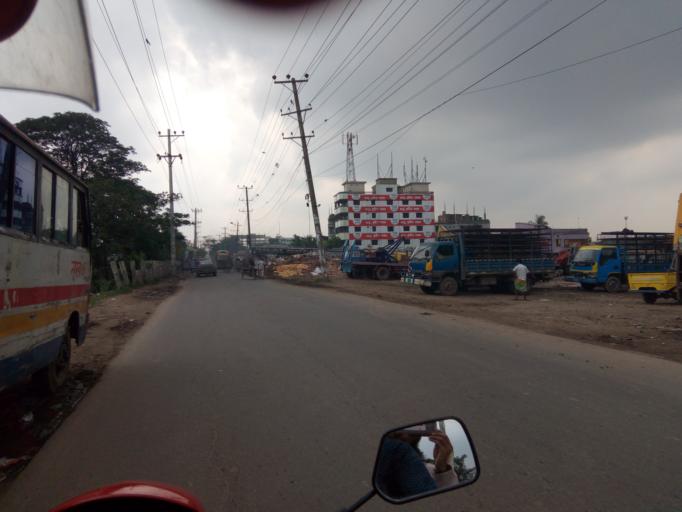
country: BD
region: Dhaka
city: Paltan
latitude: 23.7147
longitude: 90.4573
